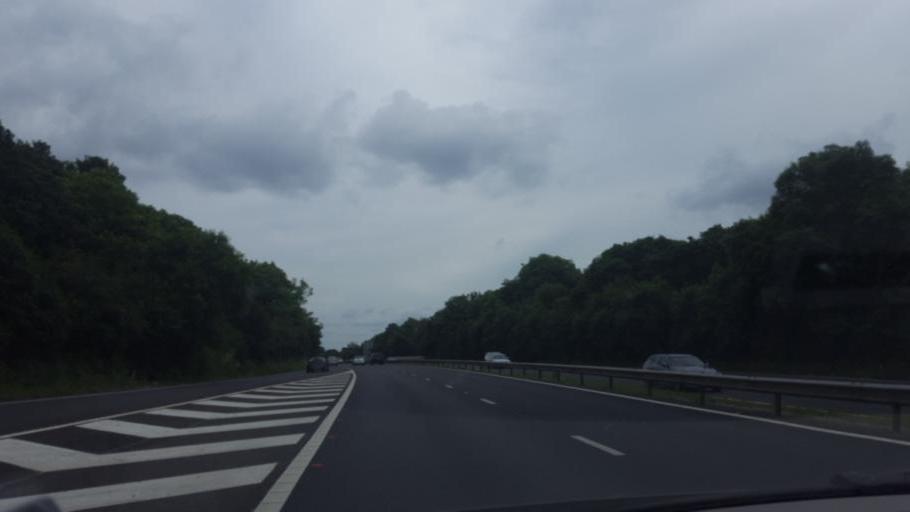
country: GB
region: England
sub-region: Royal Borough of Windsor and Maidenhead
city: White Waltham
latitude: 51.5171
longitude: -0.7632
